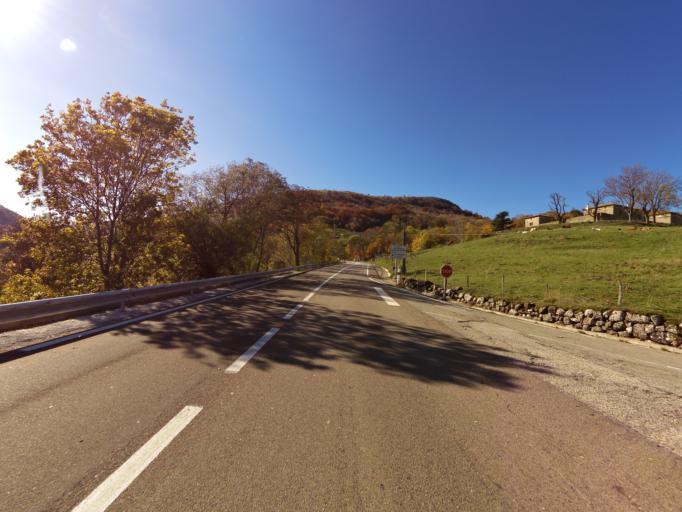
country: FR
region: Rhone-Alpes
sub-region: Departement de l'Ardeche
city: Saint-Priest
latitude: 44.7271
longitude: 4.4991
